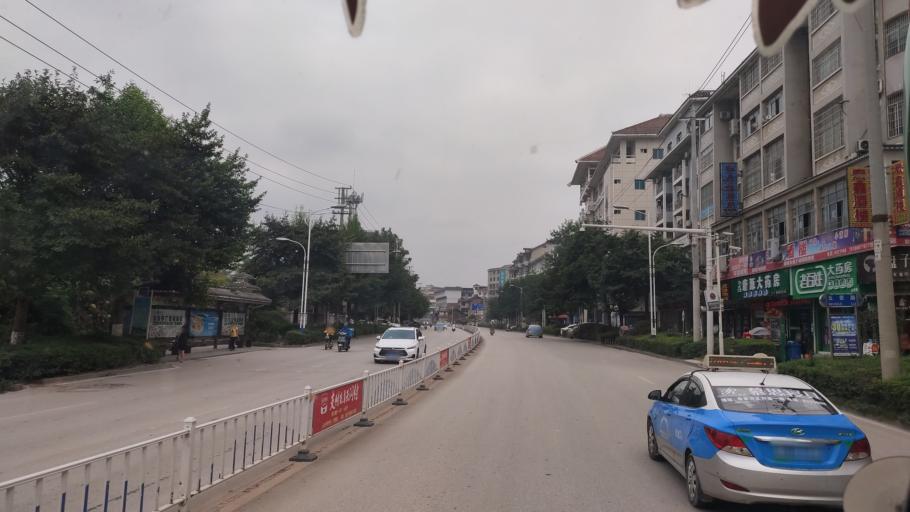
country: CN
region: Guizhou Sheng
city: Zhongchao
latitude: 26.2149
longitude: 109.1168
